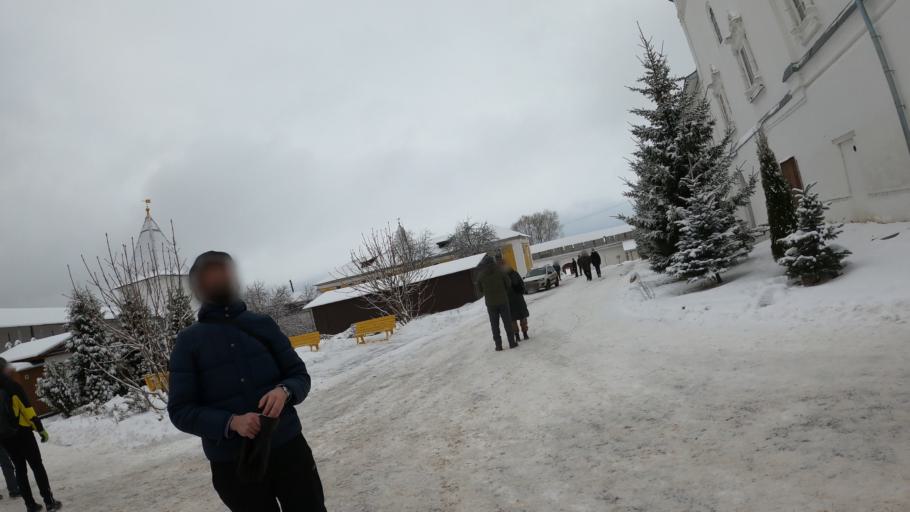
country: RU
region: Jaroslavl
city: Pereslavl'-Zalesskiy
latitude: 56.7608
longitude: 38.8593
